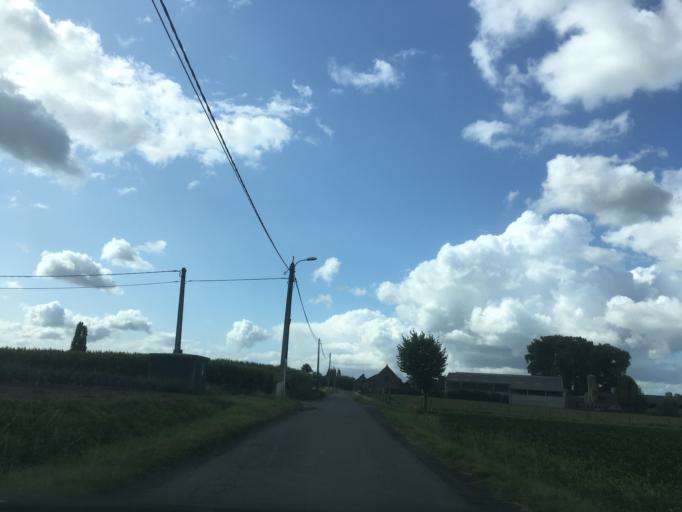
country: BE
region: Flanders
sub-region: Provincie West-Vlaanderen
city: Kortemark
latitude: 51.0173
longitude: 3.0552
